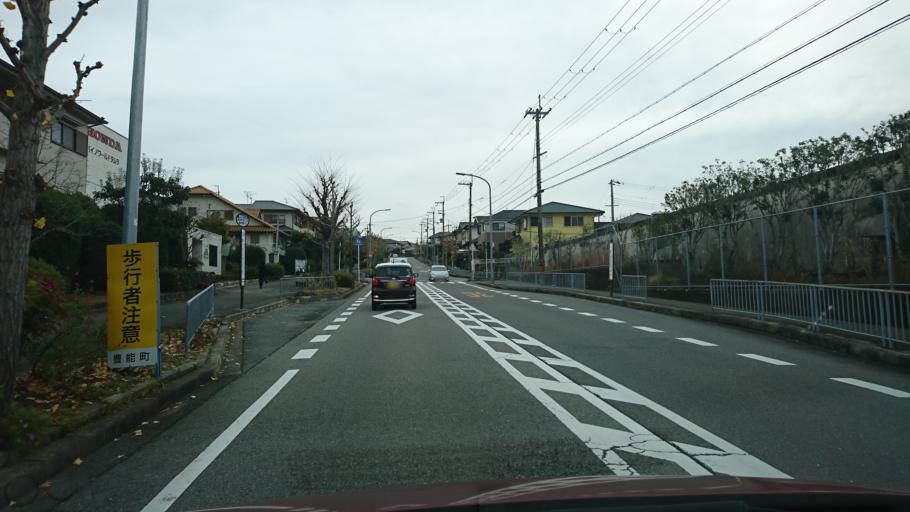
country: JP
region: Osaka
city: Mino
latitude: 34.9000
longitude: 135.4464
